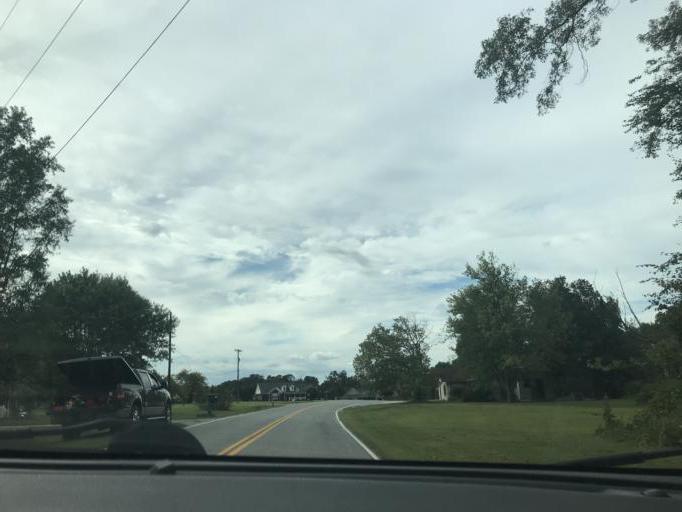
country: US
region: North Carolina
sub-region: Cleveland County
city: Boiling Springs
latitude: 35.1598
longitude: -81.7042
